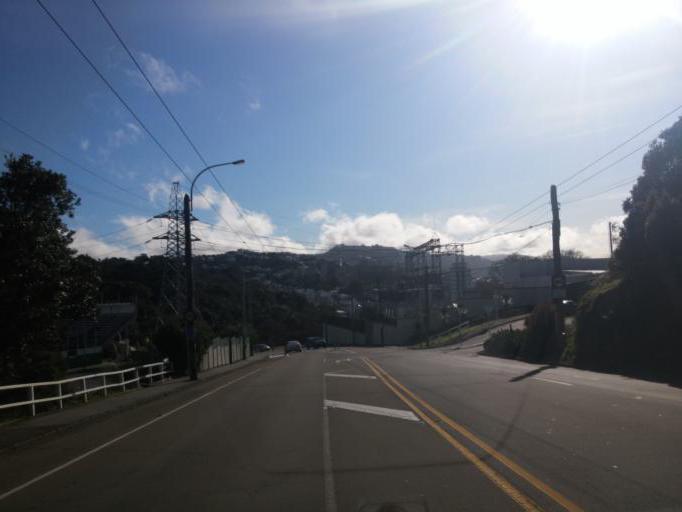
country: NZ
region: Wellington
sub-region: Wellington City
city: Wellington
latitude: -41.3016
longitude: 174.7695
